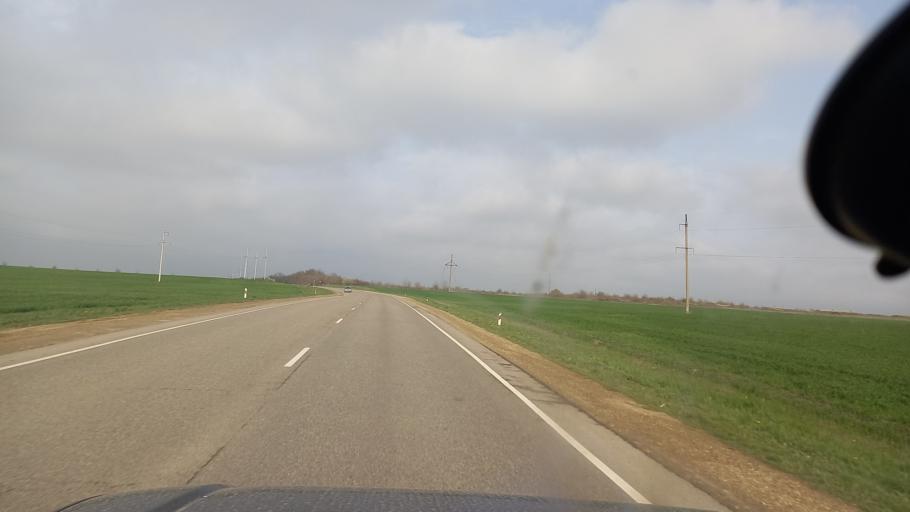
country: RU
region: Krasnodarskiy
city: Varenikovskaya
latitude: 45.1009
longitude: 37.6016
